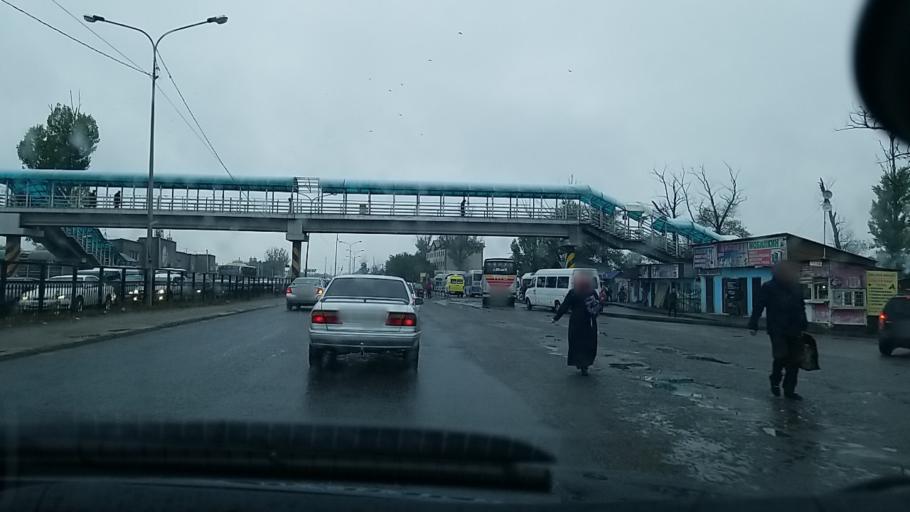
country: KZ
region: Almaty Oblysy
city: Burunday
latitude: 43.2308
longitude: 76.7733
